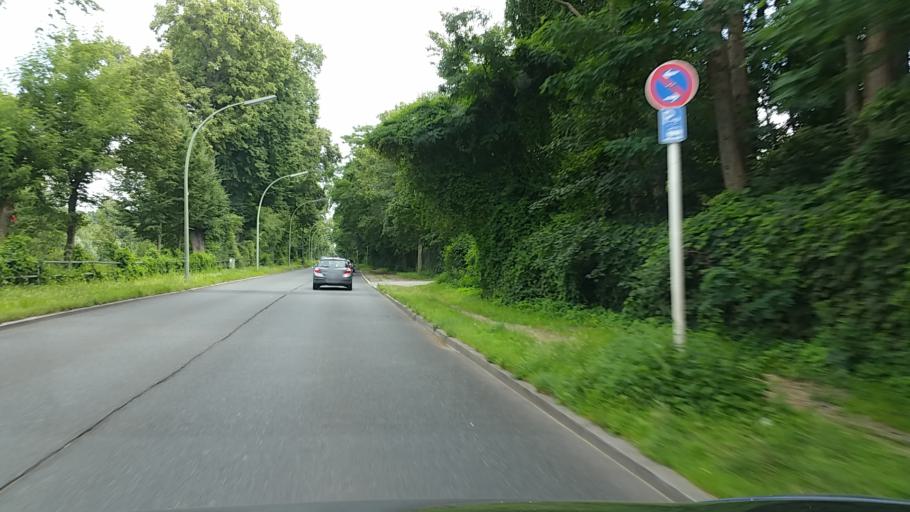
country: DE
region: Berlin
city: Siemensstadt
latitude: 52.5485
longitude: 13.2757
